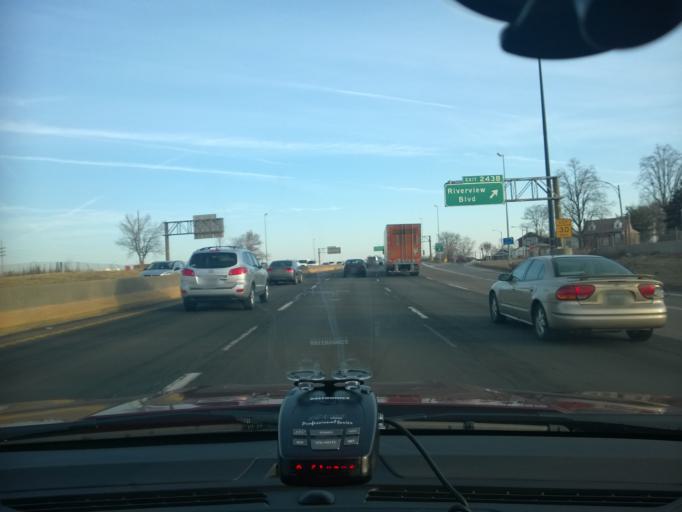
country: US
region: Missouri
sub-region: Saint Louis County
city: Pine Lawn
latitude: 38.6951
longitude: -90.2604
